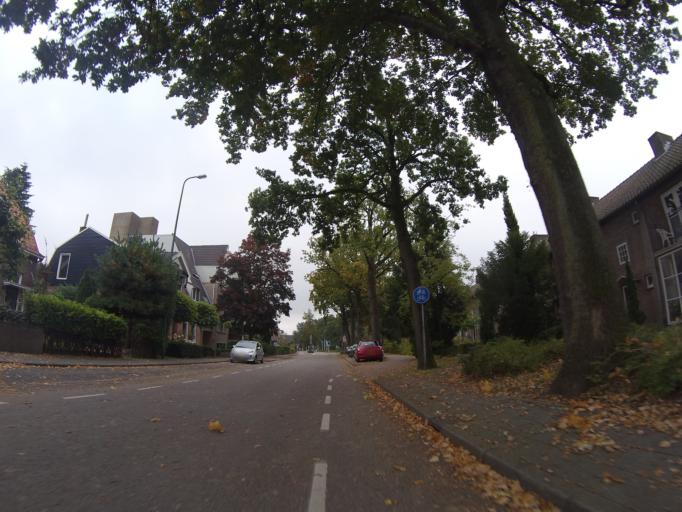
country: NL
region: Utrecht
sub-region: Gemeente Amersfoort
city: Randenbroek
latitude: 52.1425
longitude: 5.3930
